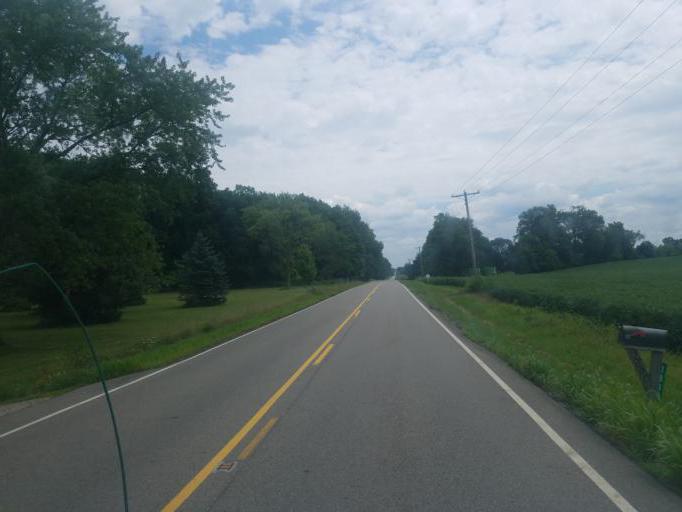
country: US
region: Ohio
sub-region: Licking County
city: Utica
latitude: 40.2021
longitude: -82.5323
